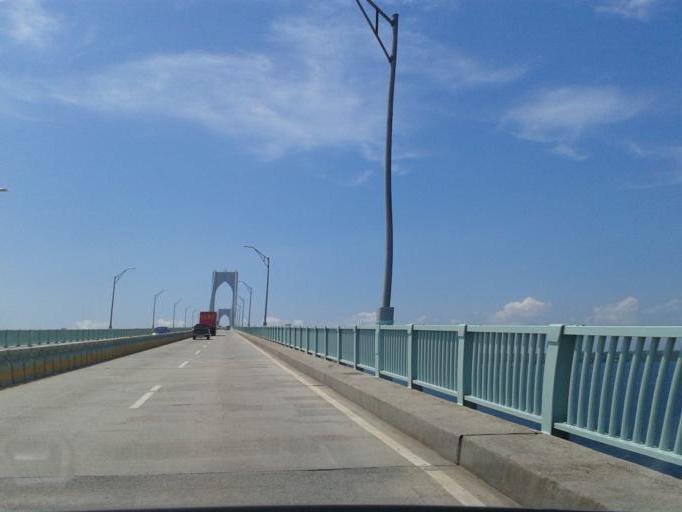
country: US
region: Rhode Island
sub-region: Newport County
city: Newport
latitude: 41.5028
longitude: -71.3382
